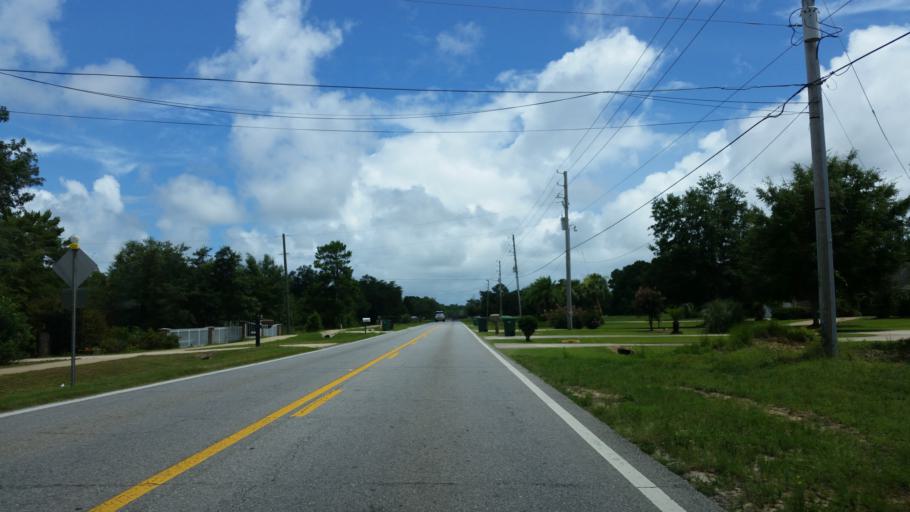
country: US
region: Florida
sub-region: Santa Rosa County
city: Holley
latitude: 30.4443
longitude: -86.9252
